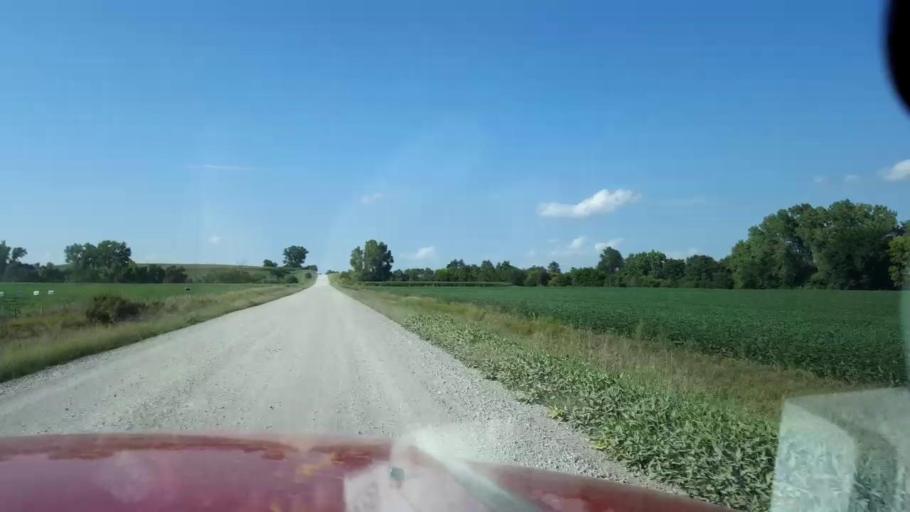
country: US
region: Iowa
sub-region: Pottawattamie County
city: Oakland
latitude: 41.2506
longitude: -95.5371
